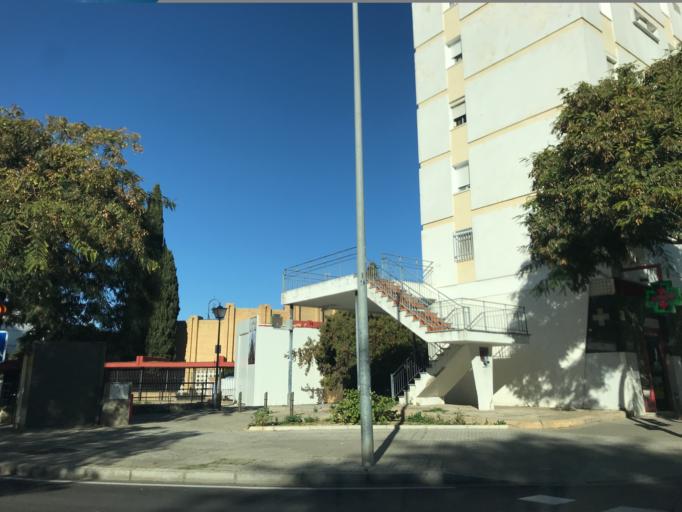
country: ES
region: Andalusia
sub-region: Provincia de Sevilla
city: Sevilla
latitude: 37.4001
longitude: -5.9565
